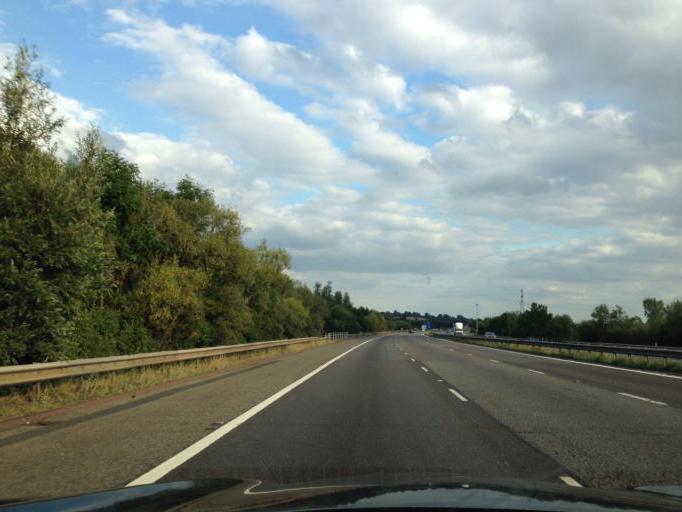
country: GB
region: England
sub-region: Oxfordshire
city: Banbury
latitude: 52.0828
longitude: -1.3233
